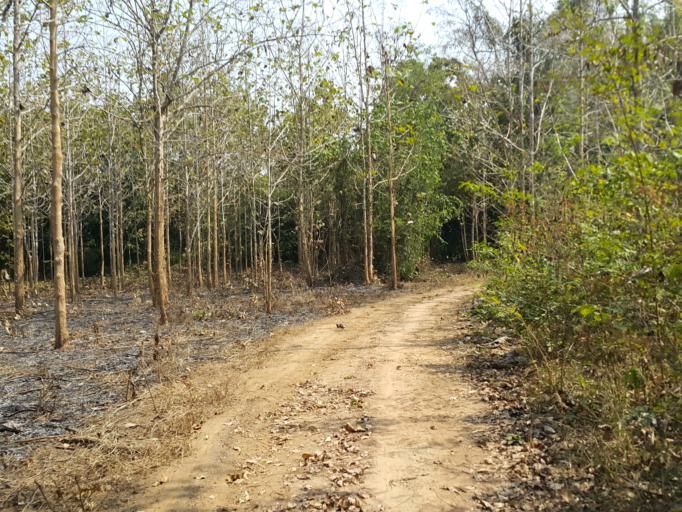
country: TH
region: Sukhothai
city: Thung Saliam
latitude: 17.3265
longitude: 99.4937
